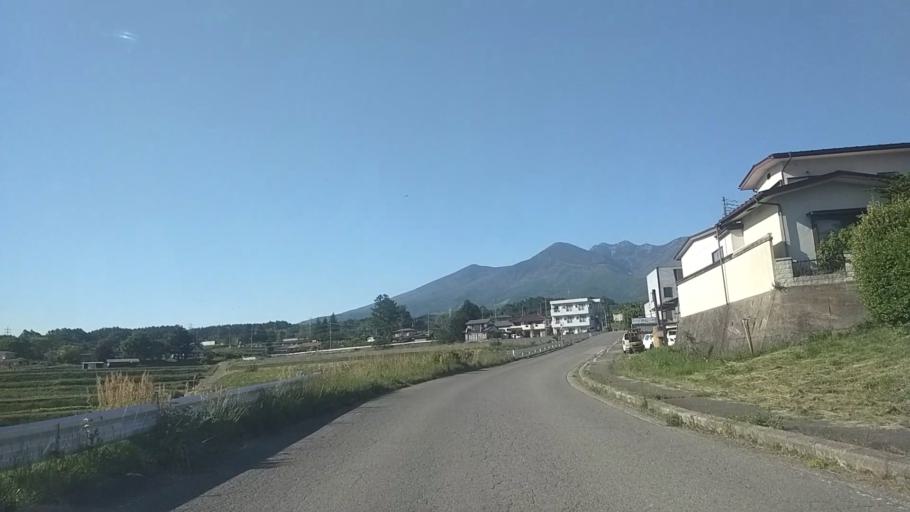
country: JP
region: Nagano
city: Chino
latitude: 35.8655
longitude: 138.3121
